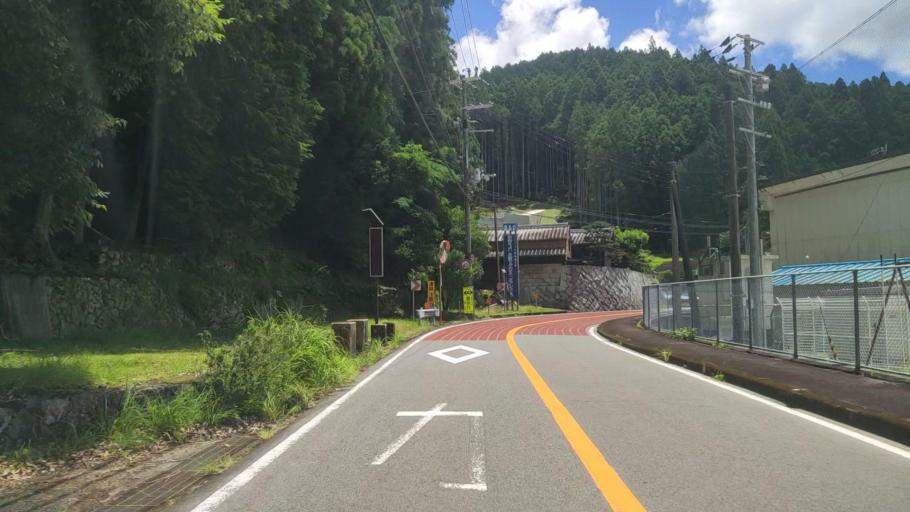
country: JP
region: Mie
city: Owase
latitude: 33.9486
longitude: 136.0766
